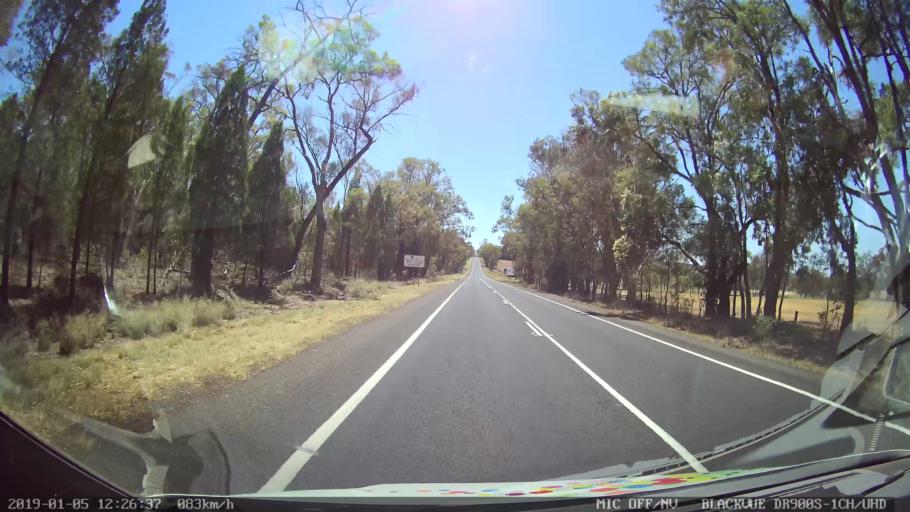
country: AU
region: New South Wales
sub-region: Warrumbungle Shire
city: Coonabarabran
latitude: -31.2533
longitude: 149.2978
